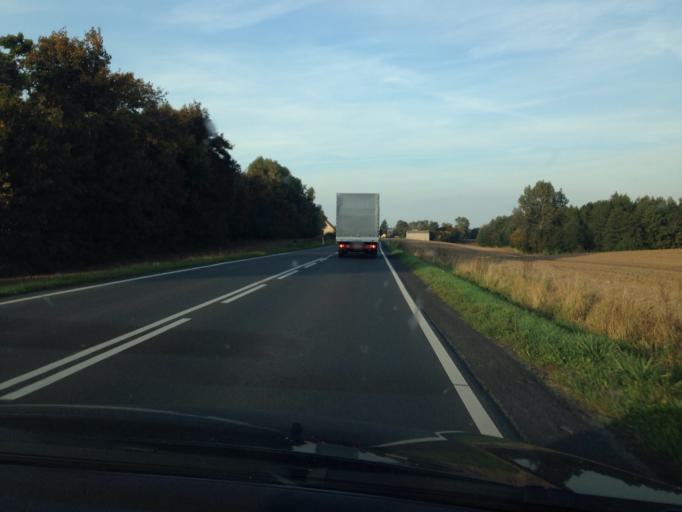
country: PL
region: Kujawsko-Pomorskie
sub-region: Powiat mogilenski
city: Mogilno
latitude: 52.6031
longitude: 17.8976
